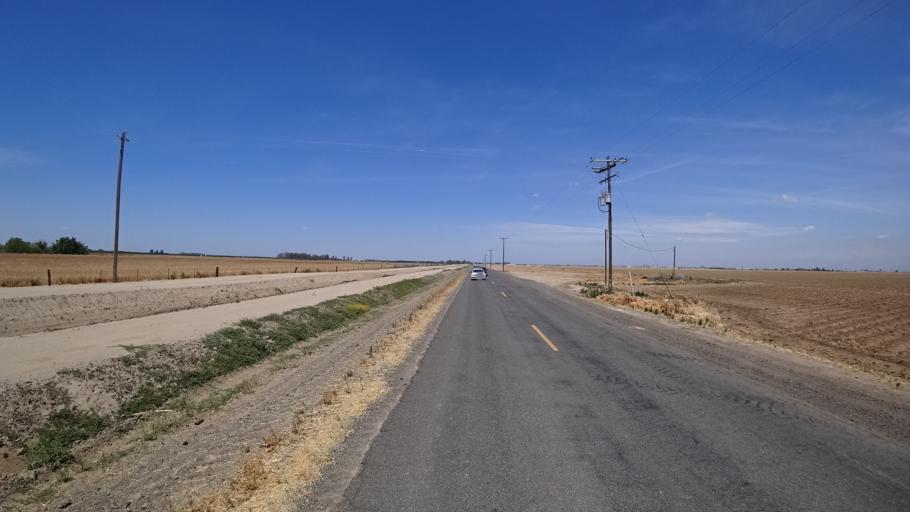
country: US
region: California
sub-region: Kings County
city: Home Garden
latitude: 36.2372
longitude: -119.6728
